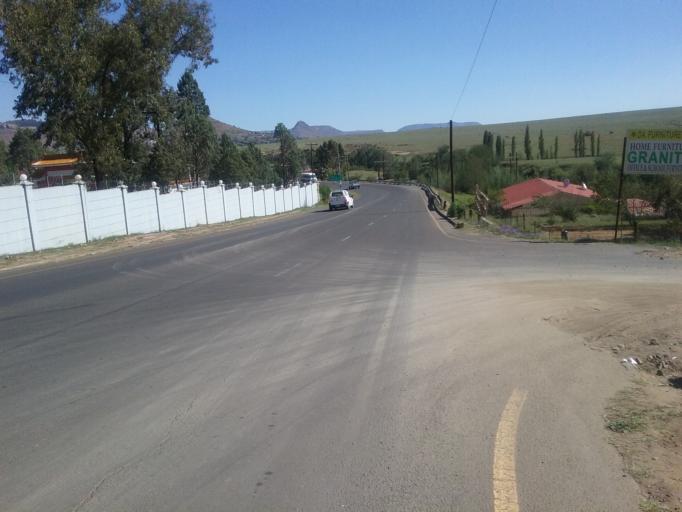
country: LS
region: Maseru
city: Maseru
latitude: -29.3067
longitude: 27.4654
